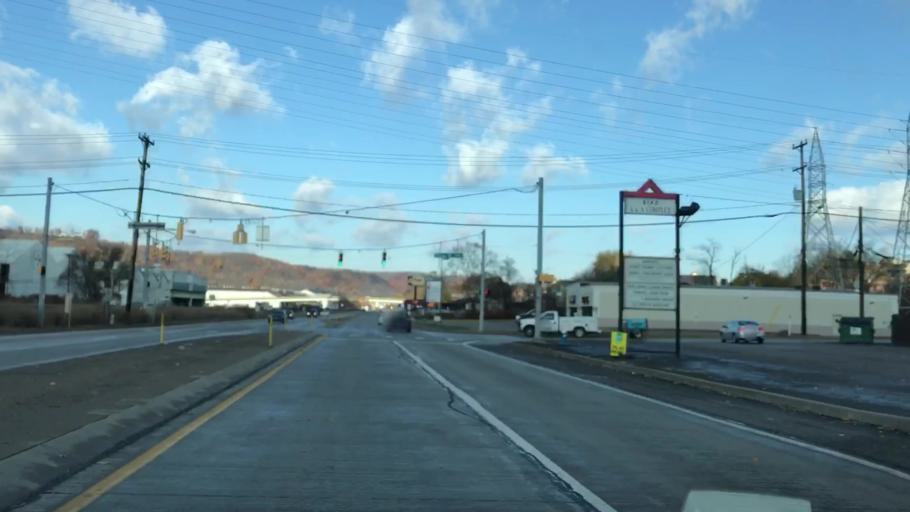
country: US
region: Pennsylvania
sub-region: Beaver County
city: Ambridge
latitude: 40.5764
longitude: -80.2221
